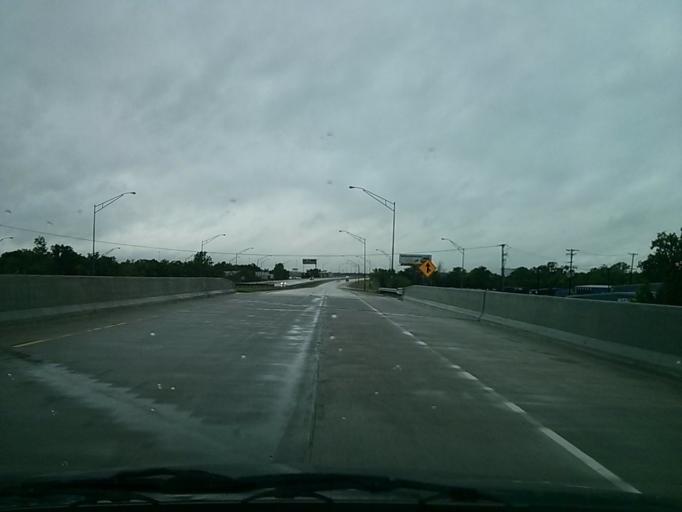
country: US
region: Oklahoma
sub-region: Tulsa County
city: Oakhurst
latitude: 36.0979
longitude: -96.0294
